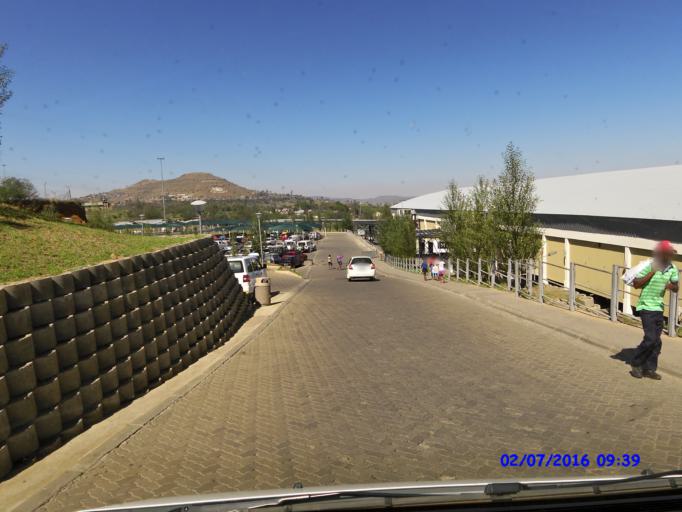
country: LS
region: Maseru
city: Maseru
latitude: -29.3170
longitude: 27.4793
